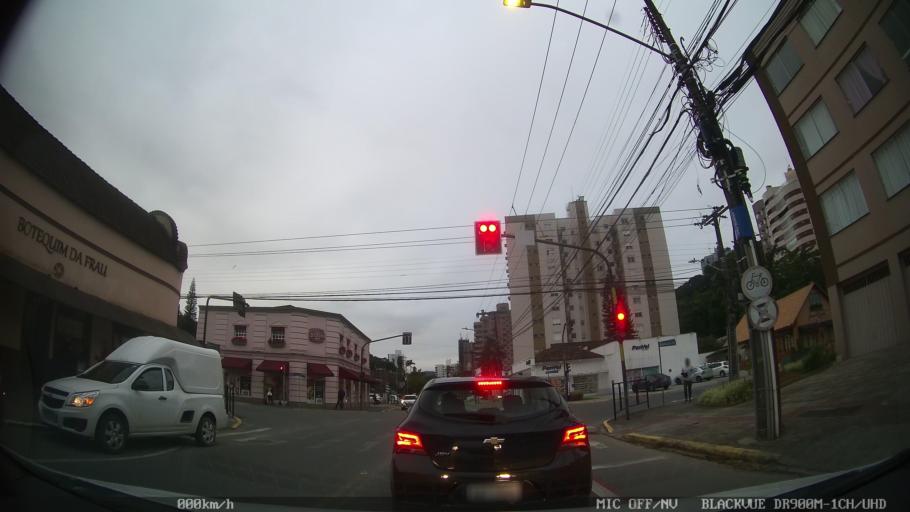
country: BR
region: Santa Catarina
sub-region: Joinville
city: Joinville
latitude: -26.3033
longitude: -48.8595
